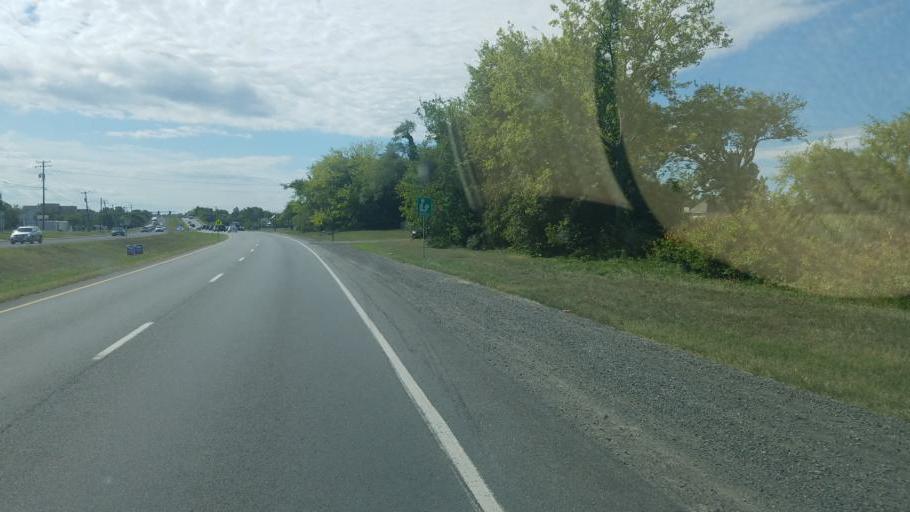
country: US
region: Virginia
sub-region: Fauquier County
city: Bealeton
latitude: 38.5785
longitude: -77.7667
